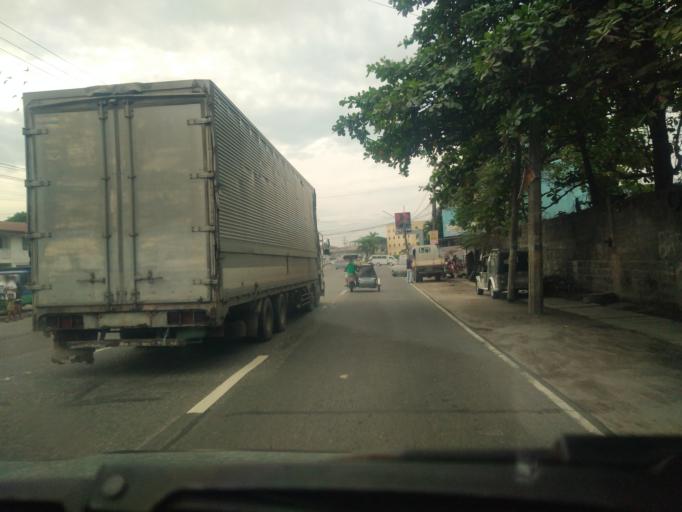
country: PH
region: Central Luzon
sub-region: Province of Pampanga
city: San Fernando
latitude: 15.0240
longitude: 120.6978
